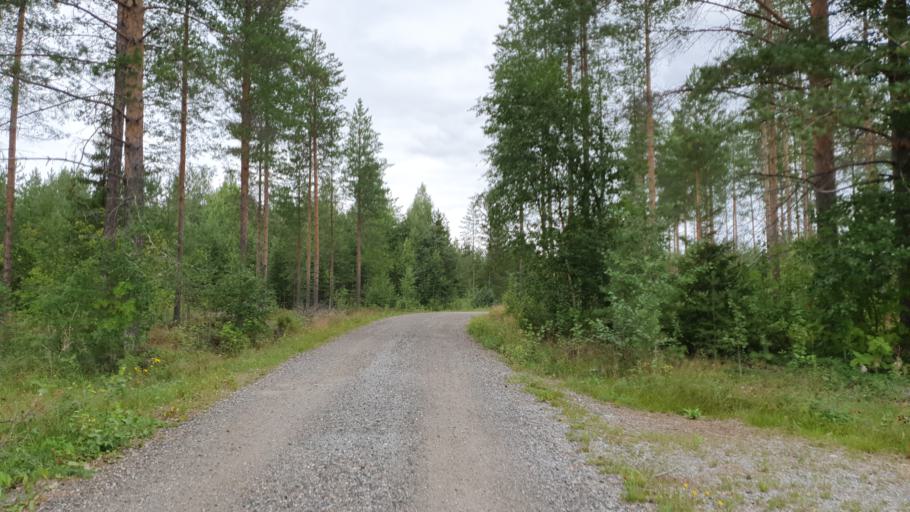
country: FI
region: Kainuu
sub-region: Kehys-Kainuu
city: Kuhmo
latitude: 64.1264
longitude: 29.4594
